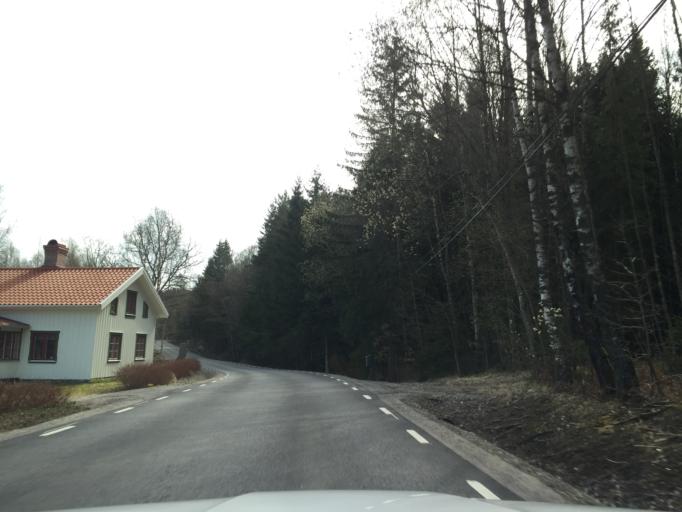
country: SE
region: Vaestra Goetaland
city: Svanesund
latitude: 58.0794
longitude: 11.9648
